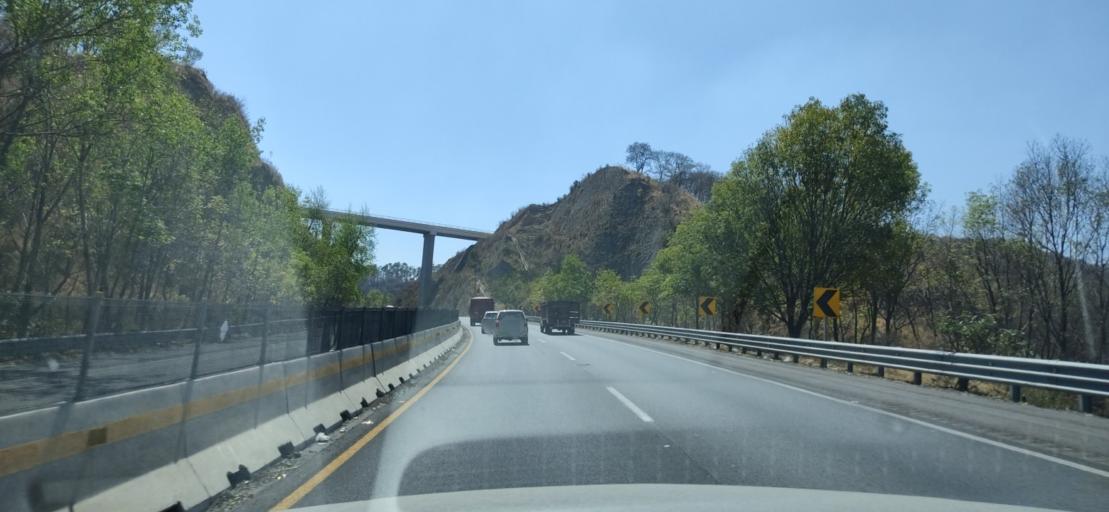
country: MX
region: Mexico
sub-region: Naucalpan de Juarez
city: La Rosa
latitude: 19.4791
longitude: -99.3135
